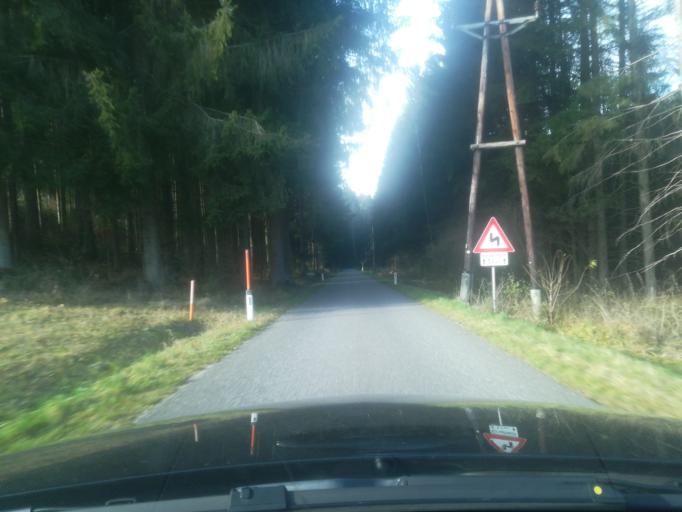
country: AT
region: Upper Austria
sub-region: Politischer Bezirk Perg
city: Perg
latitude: 48.3207
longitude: 14.6622
